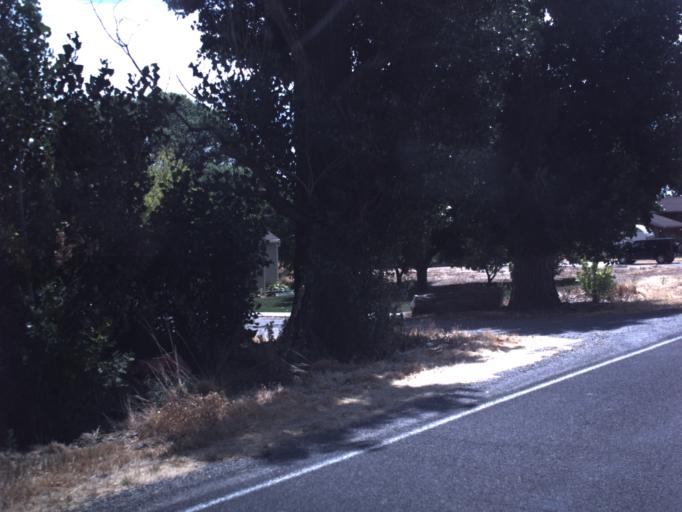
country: US
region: Utah
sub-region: Box Elder County
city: Tremonton
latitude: 41.6844
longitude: -112.2970
